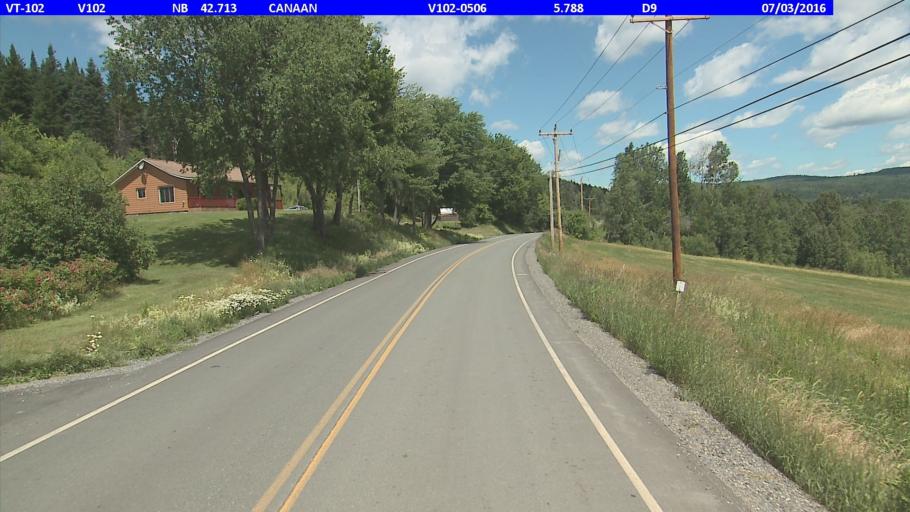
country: US
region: New Hampshire
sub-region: Coos County
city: Colebrook
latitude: 44.9821
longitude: -71.5432
